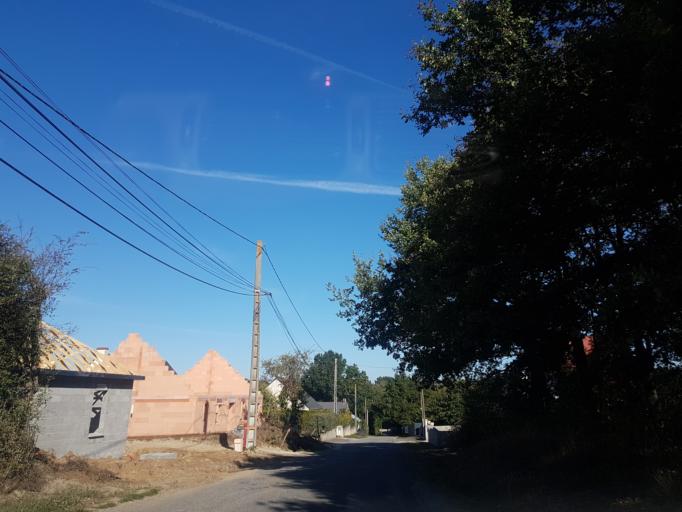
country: FR
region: Pays de la Loire
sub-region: Departement de la Loire-Atlantique
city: Petit-Mars
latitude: 47.3904
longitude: -1.4445
